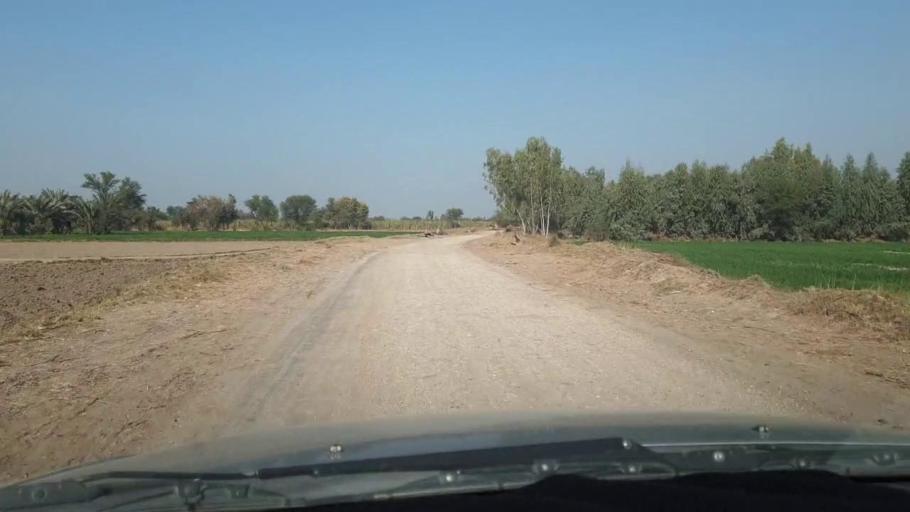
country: PK
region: Sindh
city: Mirpur Mathelo
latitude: 27.9187
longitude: 69.5566
